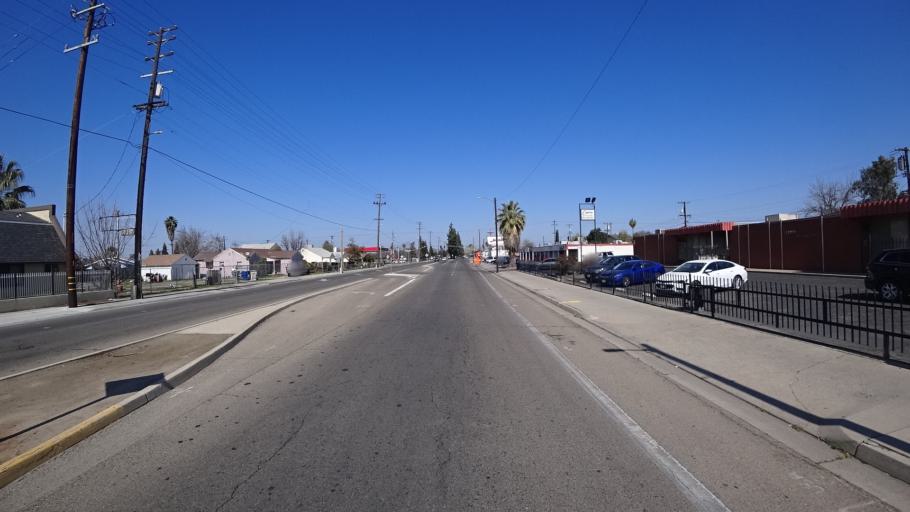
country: US
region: California
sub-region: Fresno County
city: Fresno
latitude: 36.7632
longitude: -119.8267
